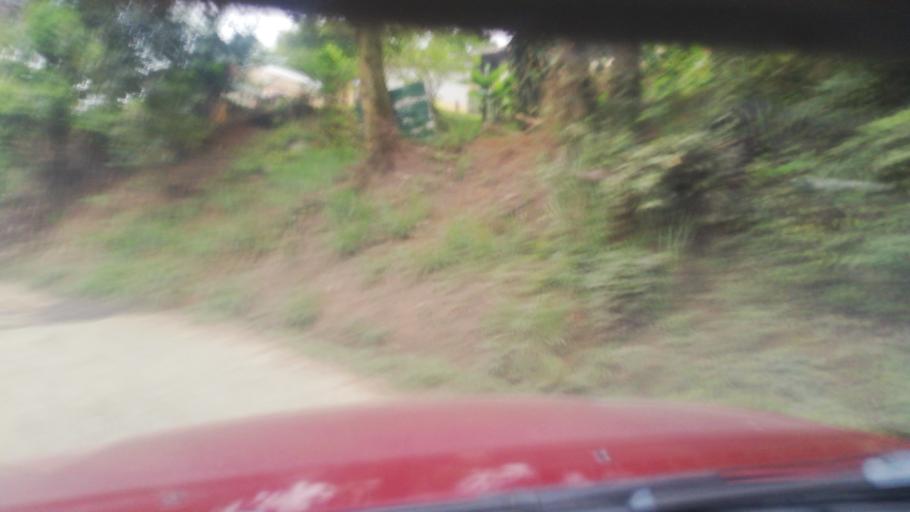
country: CO
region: Valle del Cauca
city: Cali
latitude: 3.4958
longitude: -76.5476
